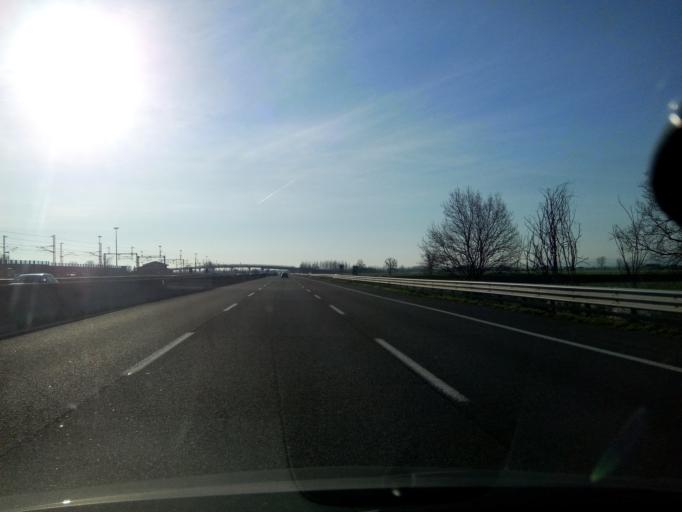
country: IT
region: Emilia-Romagna
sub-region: Provincia di Reggio Emilia
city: Campegine
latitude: 44.7609
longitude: 10.5346
